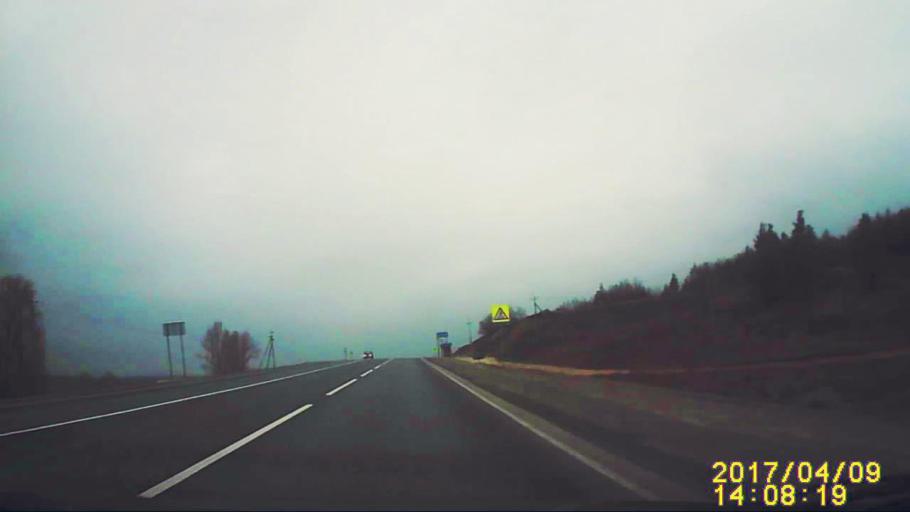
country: RU
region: Ulyanovsk
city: Silikatnyy
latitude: 54.0192
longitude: 48.2158
